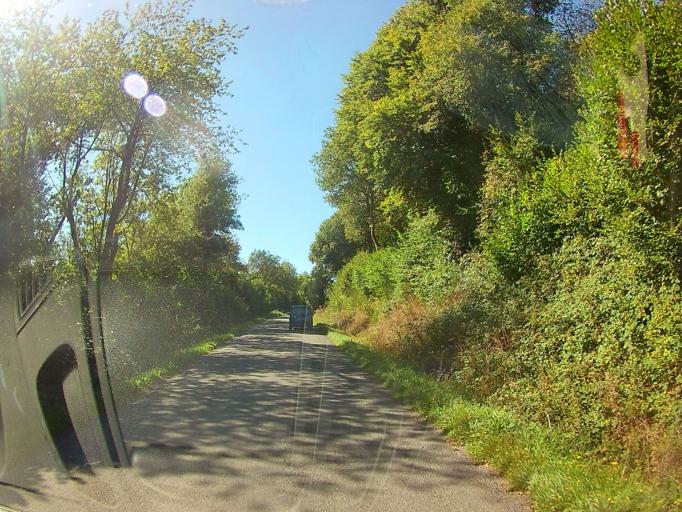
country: FR
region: Auvergne
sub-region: Departement du Puy-de-Dome
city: Manzat
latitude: 45.9196
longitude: 2.9464
